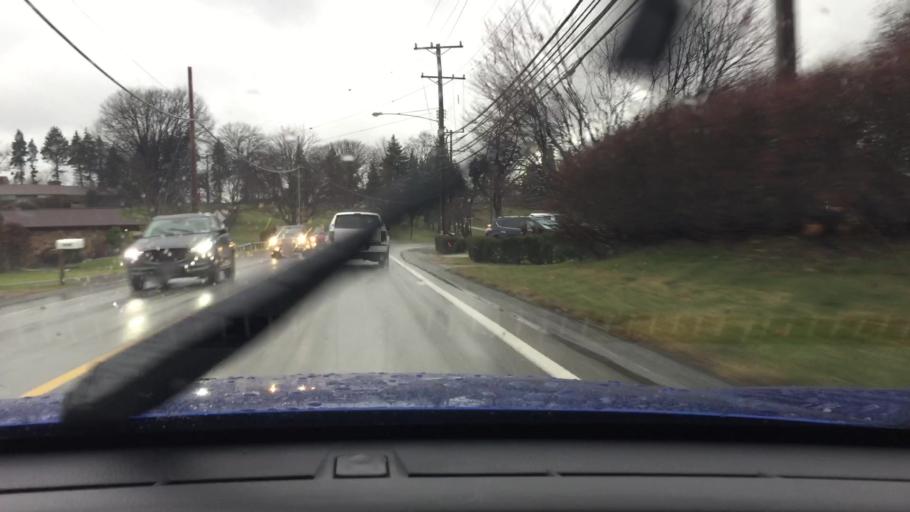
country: US
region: Pennsylvania
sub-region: Allegheny County
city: Pleasant Hills
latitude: 40.3258
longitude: -79.9287
